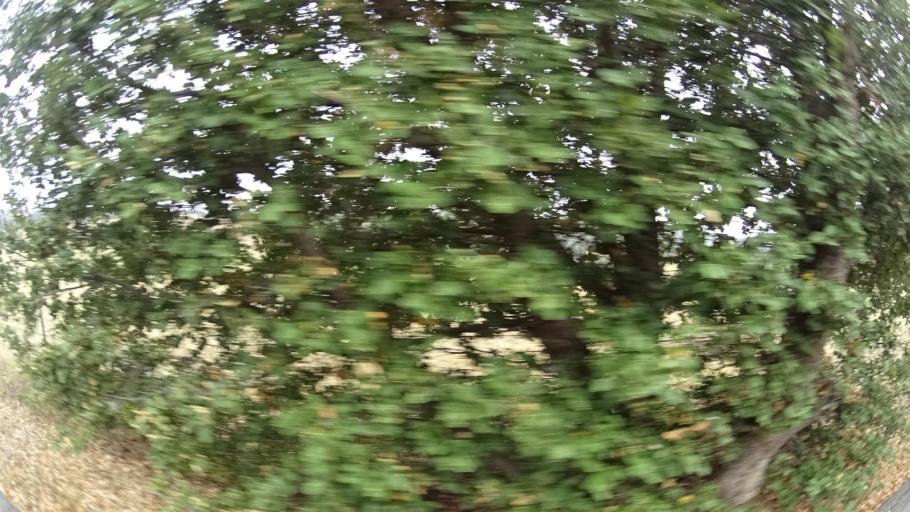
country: US
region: California
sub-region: San Diego County
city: Julian
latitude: 33.0425
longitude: -116.6023
